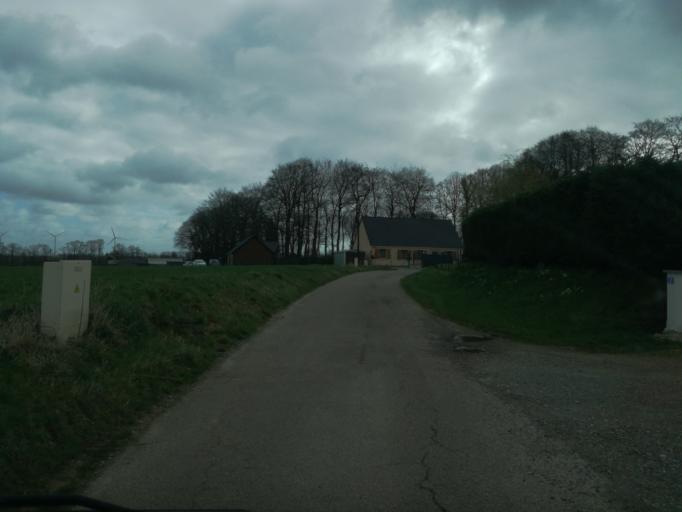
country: FR
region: Haute-Normandie
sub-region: Departement de la Seine-Maritime
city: Yebleron
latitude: 49.6754
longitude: 0.4925
